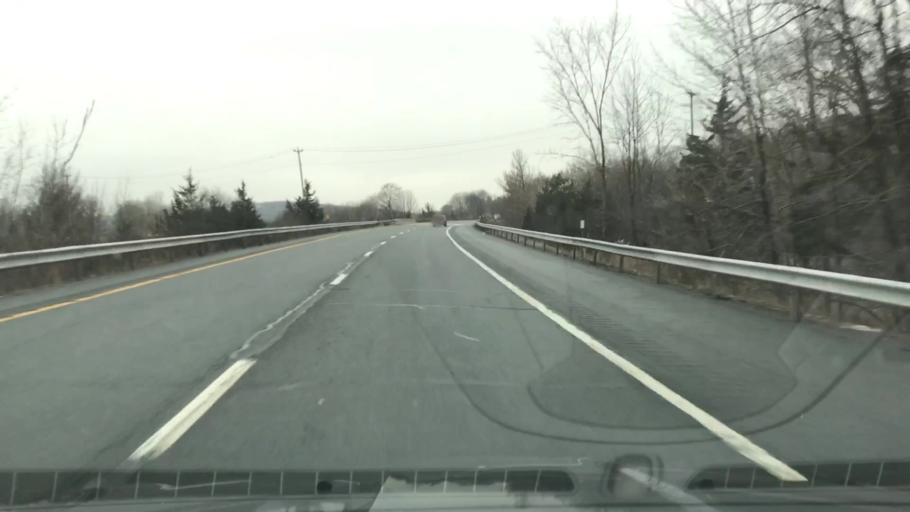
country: US
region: New York
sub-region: Orange County
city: Middletown
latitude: 41.4043
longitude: -74.4701
